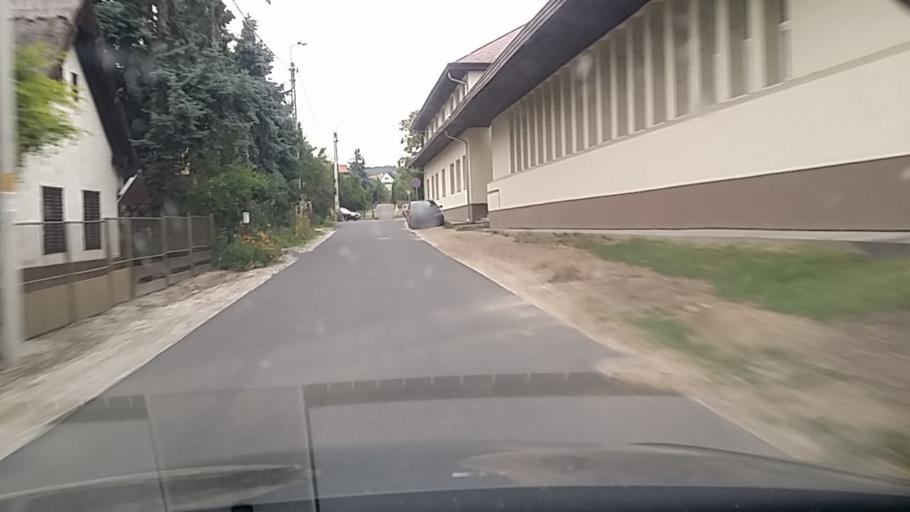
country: HU
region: Zala
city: Vonyarcvashegy
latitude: 46.7628
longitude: 17.3069
